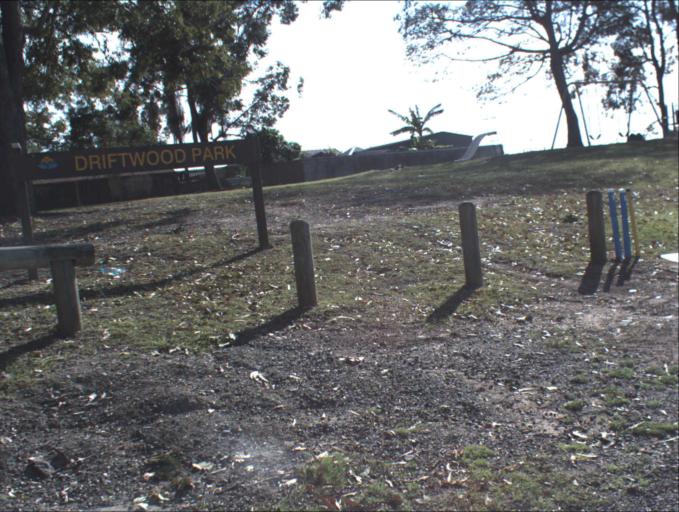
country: AU
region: Queensland
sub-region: Logan
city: Waterford West
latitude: -27.6840
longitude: 153.0979
